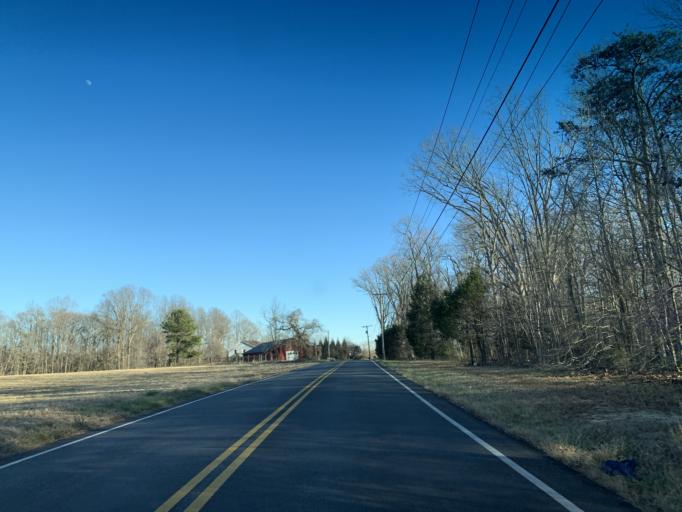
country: US
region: Maryland
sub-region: Saint Mary's County
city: Mechanicsville
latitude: 38.4685
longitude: -76.7283
